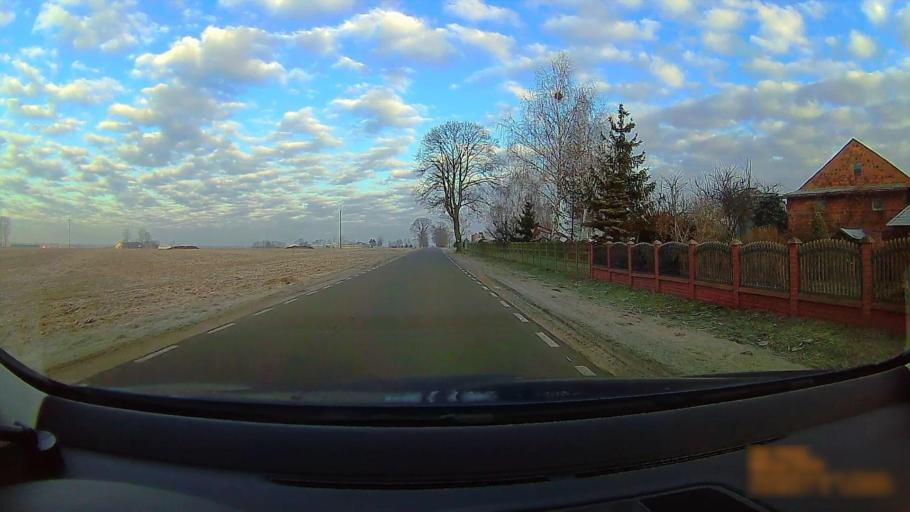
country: PL
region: Greater Poland Voivodeship
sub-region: Powiat koninski
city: Rzgow Pierwszy
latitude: 52.1094
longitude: 18.0788
